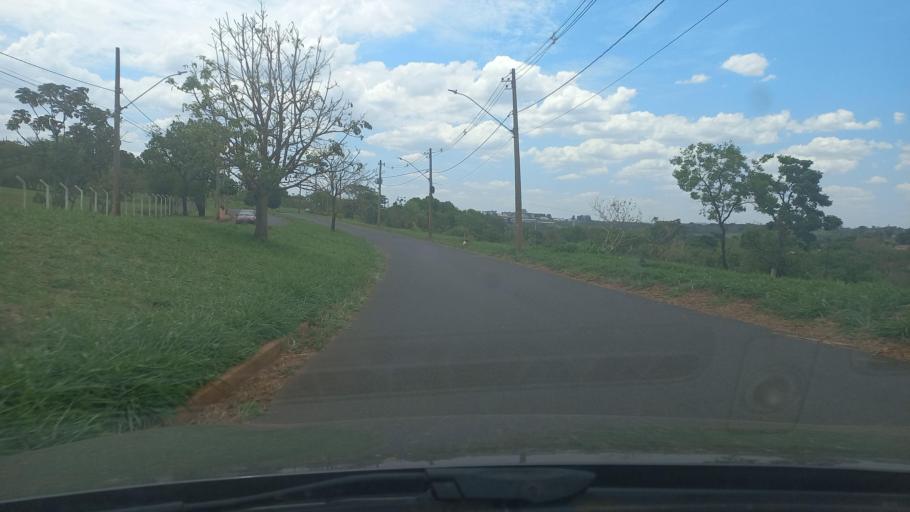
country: BR
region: Minas Gerais
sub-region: Uberaba
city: Uberaba
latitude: -19.7365
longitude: -47.9744
